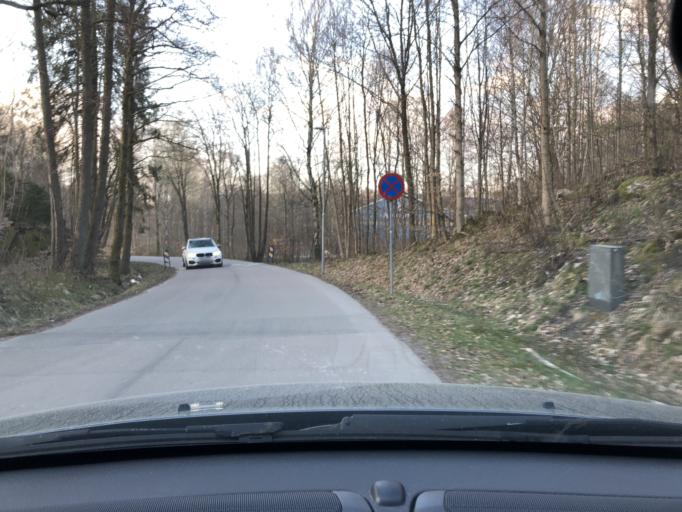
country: SE
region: Vaestra Goetaland
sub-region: Molndal
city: Moelndal
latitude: 57.6931
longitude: 12.0347
